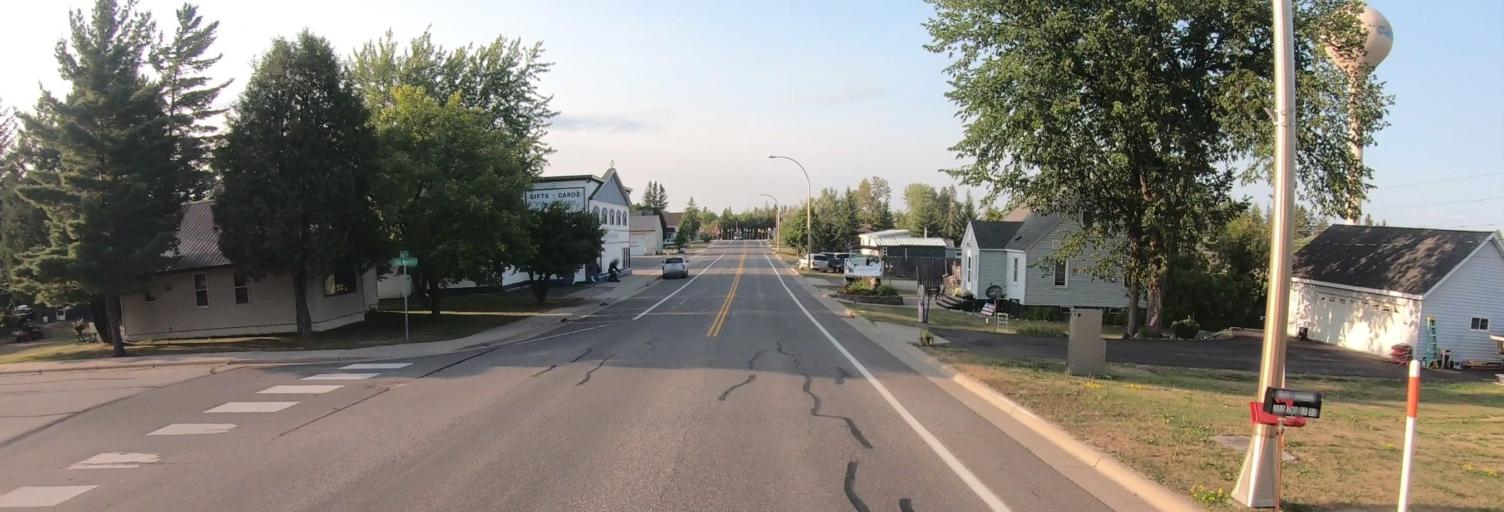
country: US
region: Minnesota
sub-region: Saint Louis County
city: Mountain Iron
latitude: 47.8500
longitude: -92.6814
